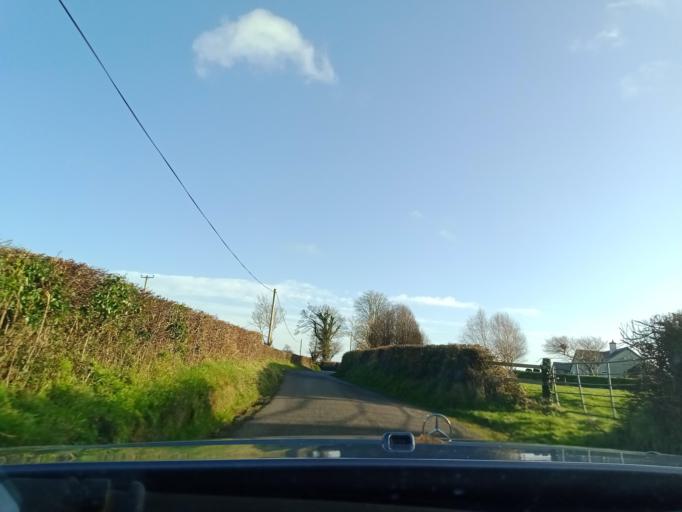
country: IE
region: Leinster
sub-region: Kilkenny
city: Callan
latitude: 52.5000
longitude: -7.3941
